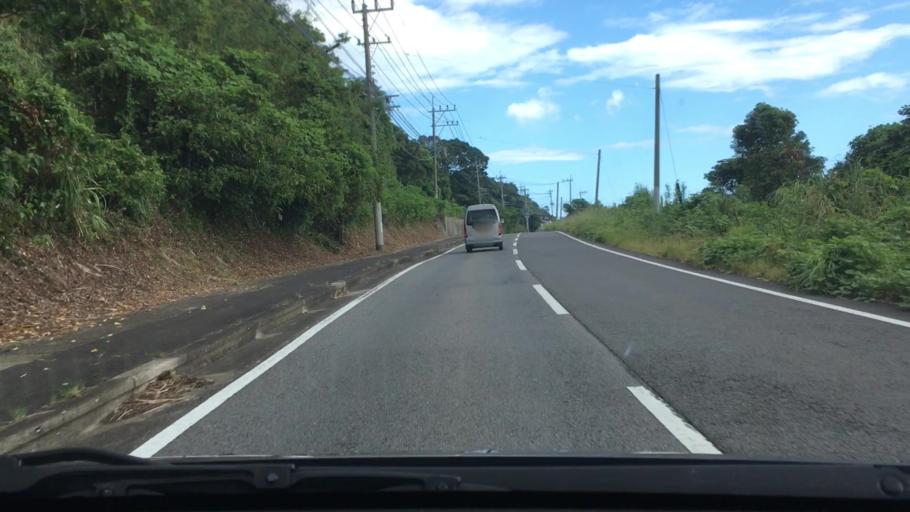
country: JP
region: Nagasaki
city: Togitsu
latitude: 32.8659
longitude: 129.6824
